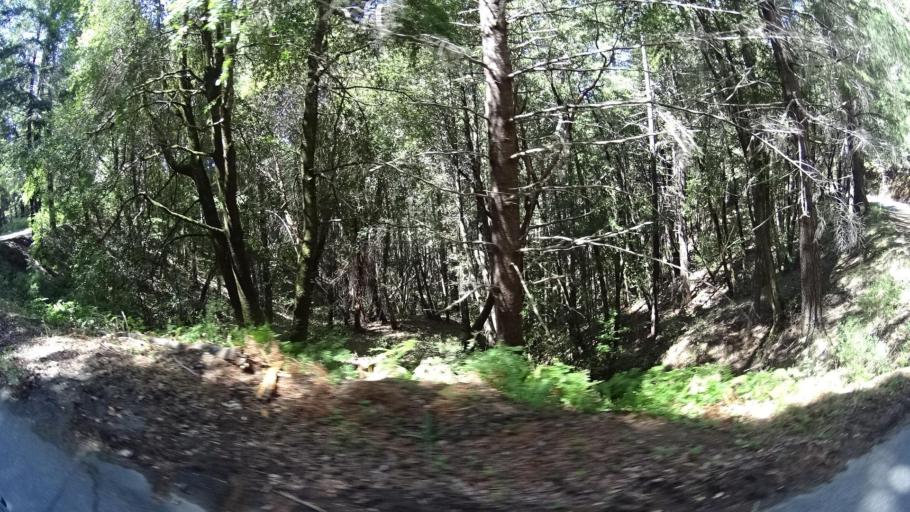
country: US
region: California
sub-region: Humboldt County
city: Redway
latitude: 40.1073
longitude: -123.9538
